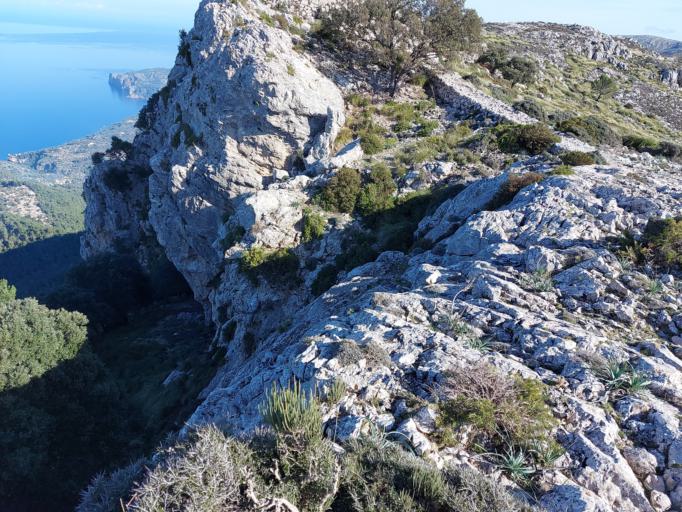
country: ES
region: Balearic Islands
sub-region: Illes Balears
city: Valldemossa
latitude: 39.7303
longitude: 2.6292
